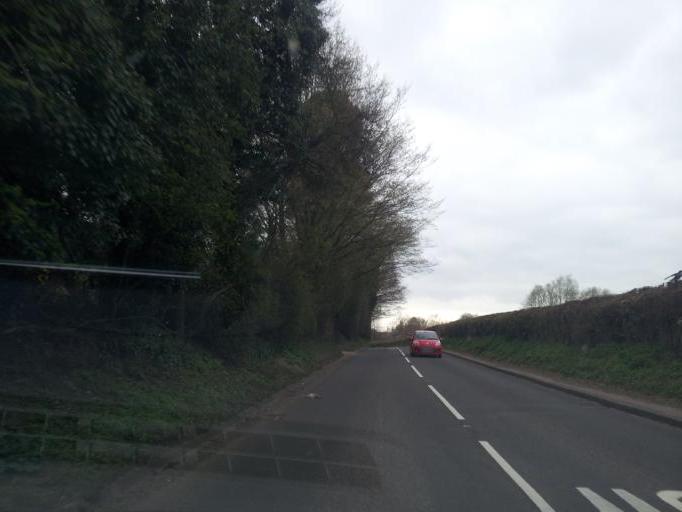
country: GB
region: England
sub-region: Hertfordshire
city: Buntingford
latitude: 51.9036
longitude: 0.0214
